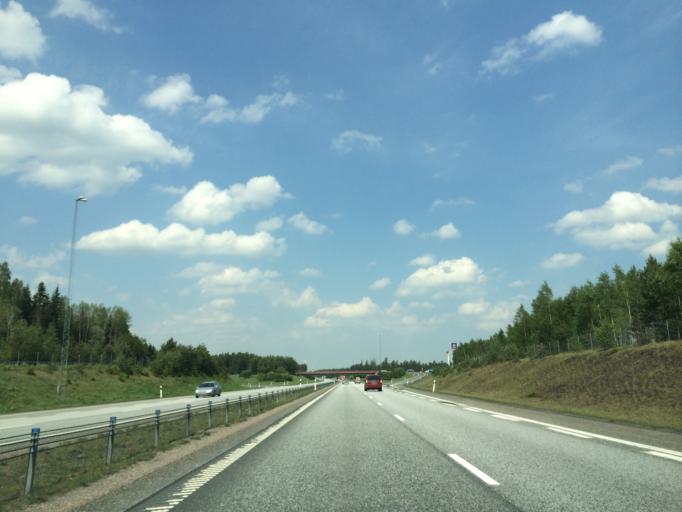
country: SE
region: Joenkoeping
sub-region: Jonkopings Kommun
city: Odensjo
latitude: 57.6626
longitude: 14.1795
